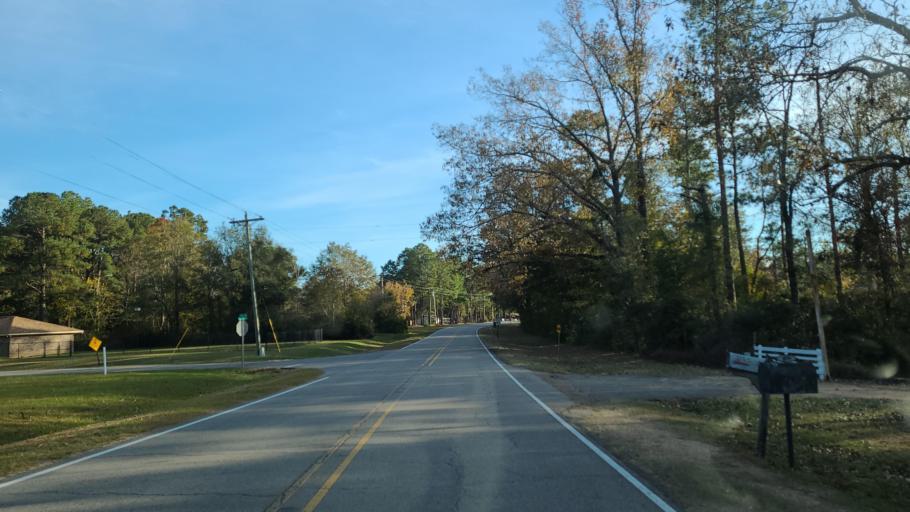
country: US
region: Mississippi
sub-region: Lamar County
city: Purvis
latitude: 31.1933
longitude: -89.2880
